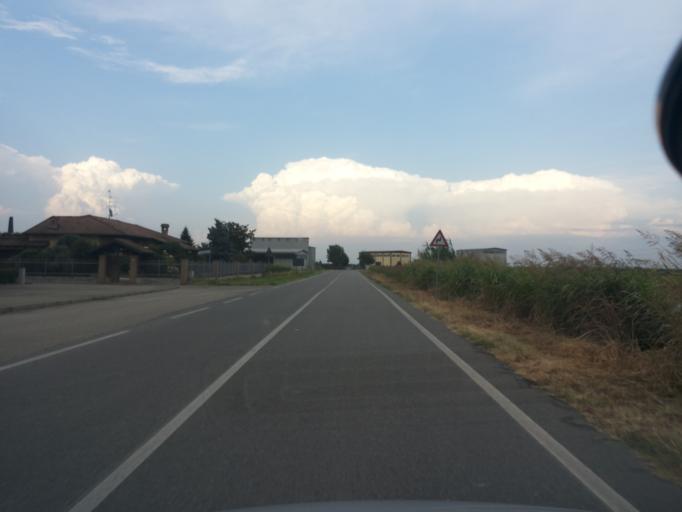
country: IT
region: Piedmont
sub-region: Provincia di Vercelli
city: Prarolo
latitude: 45.2791
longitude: 8.4773
